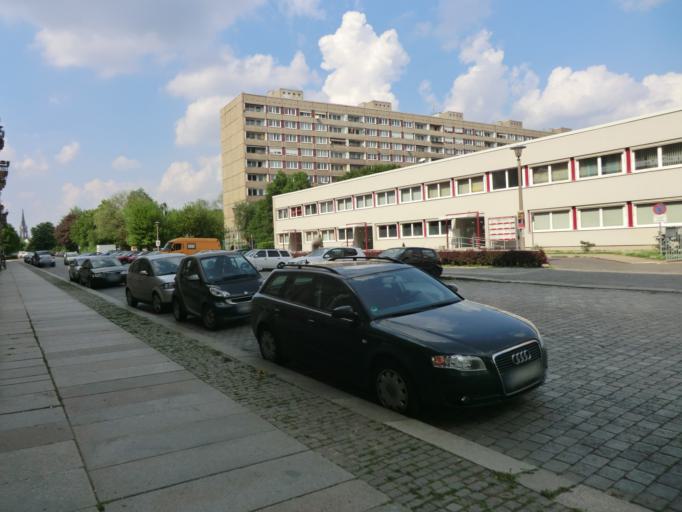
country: DE
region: Saxony
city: Dresden
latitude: 51.0561
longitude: 13.7636
